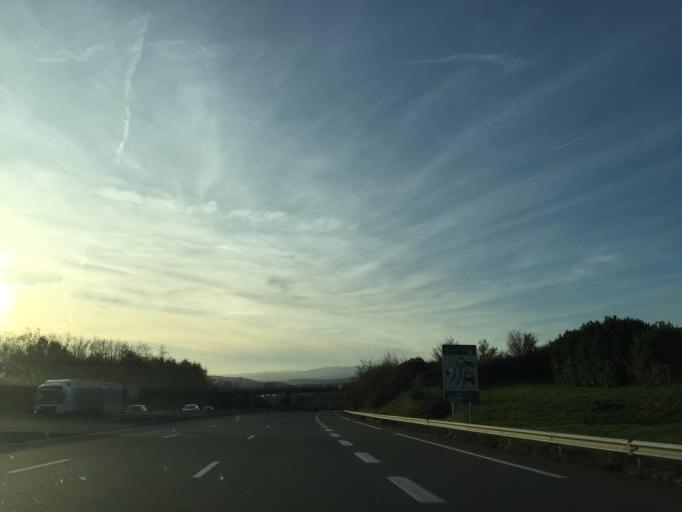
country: FR
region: Rhone-Alpes
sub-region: Departement du Rhone
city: Ternay
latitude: 45.5887
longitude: 4.8194
